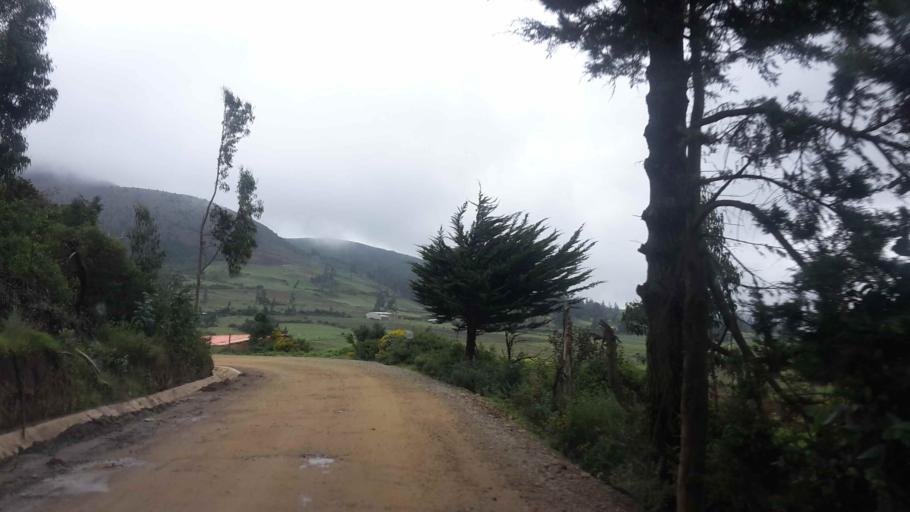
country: BO
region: Cochabamba
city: Totora
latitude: -17.5841
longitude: -65.2940
